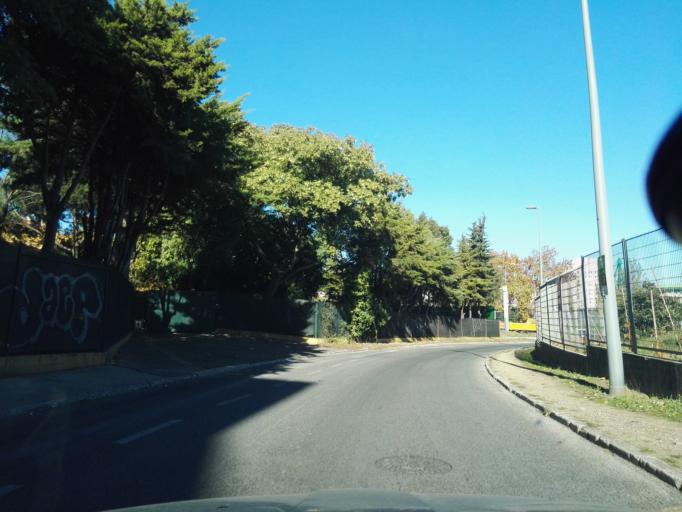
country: PT
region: Lisbon
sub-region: Odivelas
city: Olival do Basto
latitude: 38.7566
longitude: -9.1660
